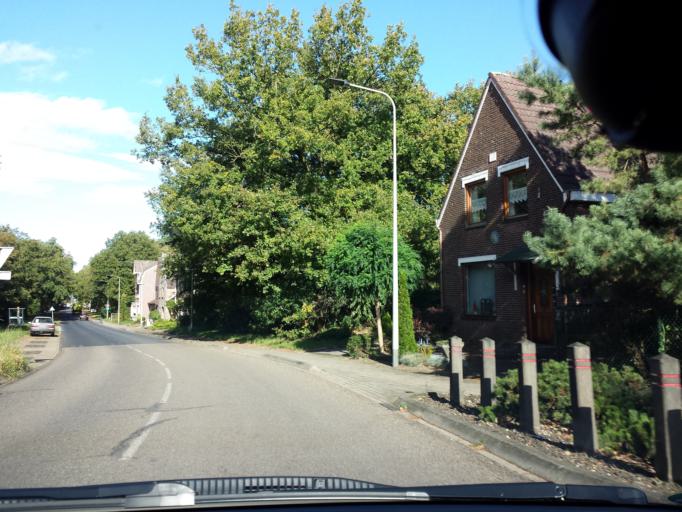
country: NL
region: Limburg
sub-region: Gemeente Onderbanken
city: Schinveld
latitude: 50.9583
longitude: 5.9900
